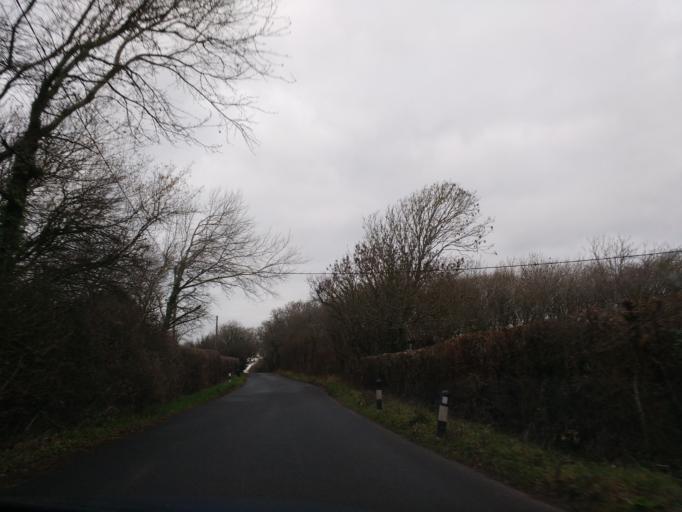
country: GB
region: England
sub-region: Isle of Wight
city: Shalfleet
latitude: 50.6944
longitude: -1.4032
